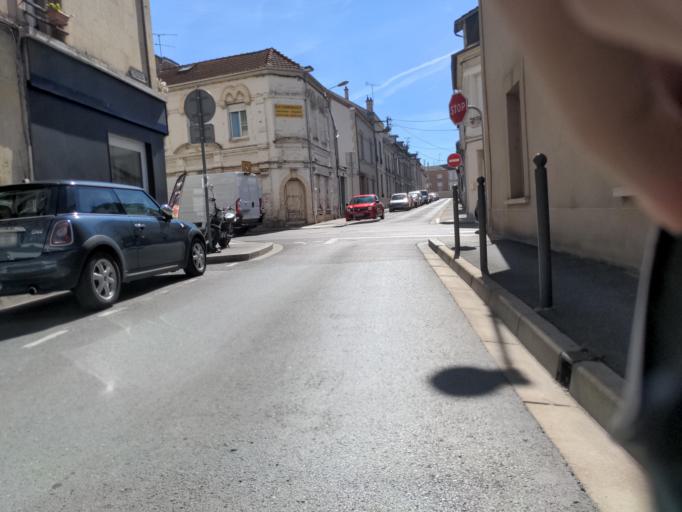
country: FR
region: Champagne-Ardenne
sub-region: Departement de la Marne
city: Reims
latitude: 49.2579
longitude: 4.0499
